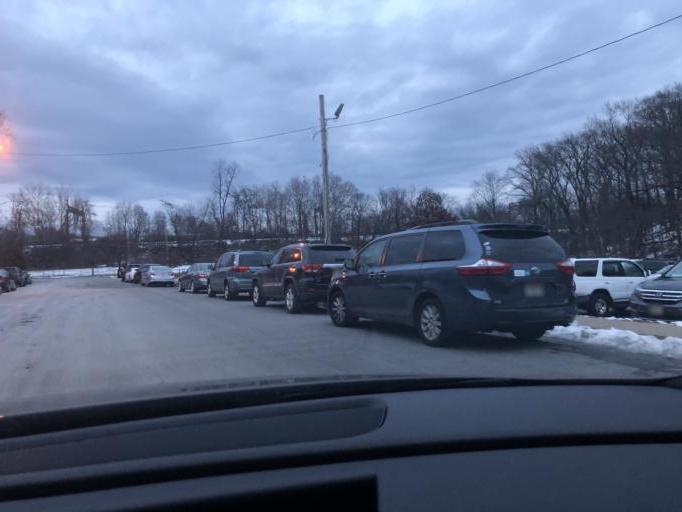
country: US
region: New Jersey
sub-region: Morris County
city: Morristown
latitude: 40.7998
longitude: -74.4781
